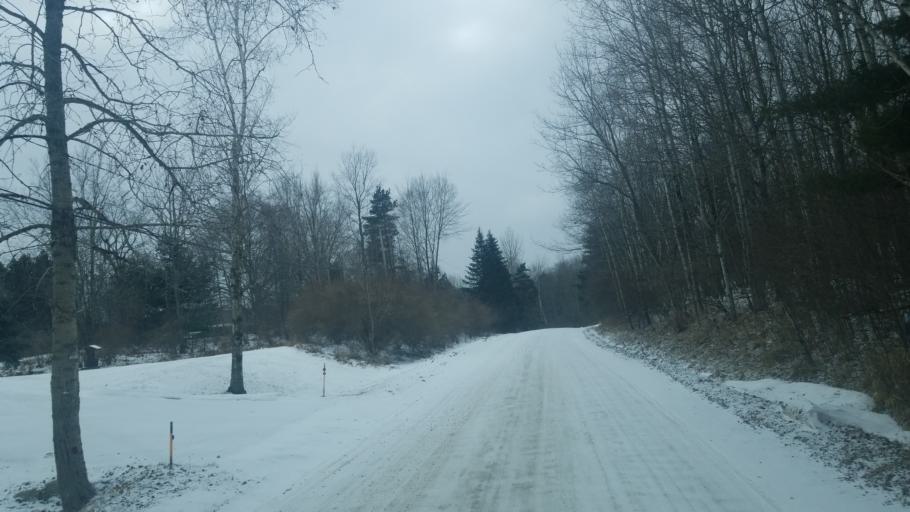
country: US
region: Michigan
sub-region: Osceola County
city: Evart
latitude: 43.8220
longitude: -85.2730
